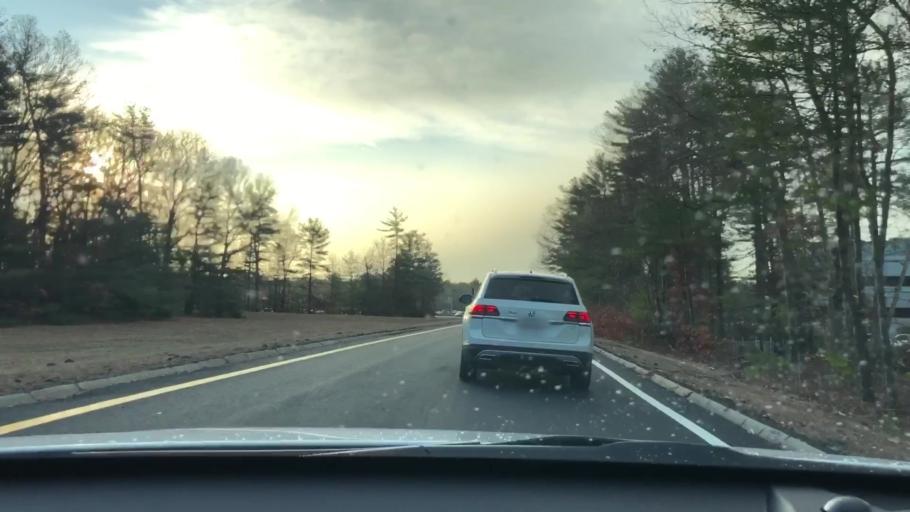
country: US
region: Massachusetts
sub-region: Plymouth County
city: Rockland
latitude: 42.1673
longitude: -70.8981
